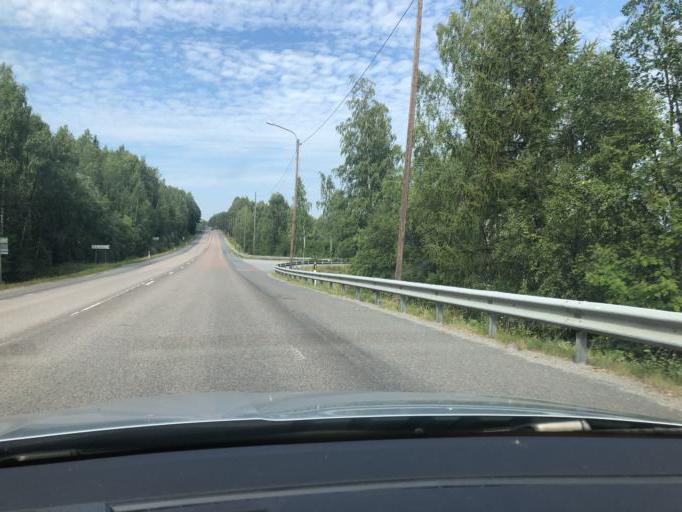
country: SE
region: Vaesternorrland
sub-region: Kramfors Kommun
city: Kramfors
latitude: 62.9488
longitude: 17.7751
